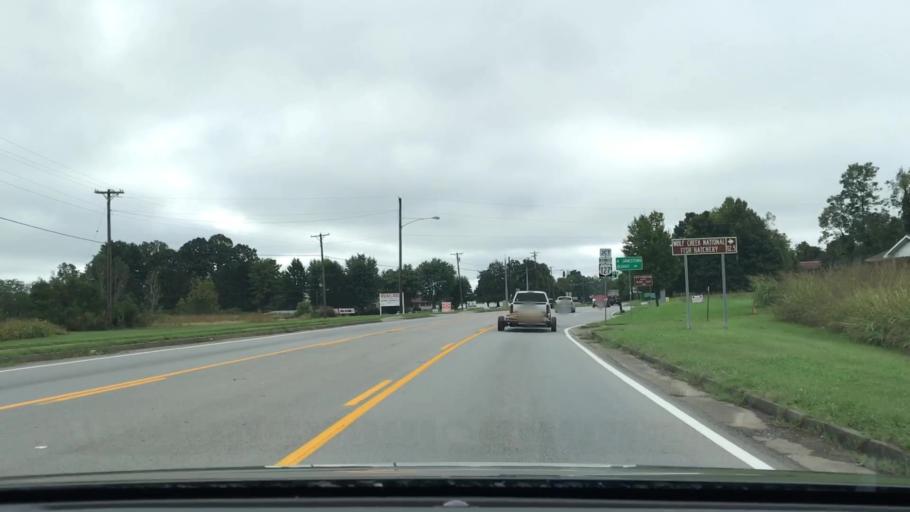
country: US
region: Kentucky
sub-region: Russell County
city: Jamestown
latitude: 36.9999
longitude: -85.0726
